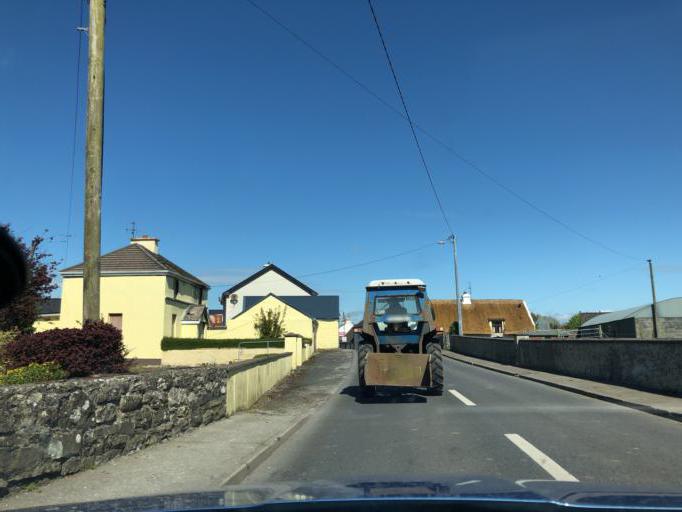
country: IE
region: Connaught
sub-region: County Galway
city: Portumna
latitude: 53.1490
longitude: -8.3725
